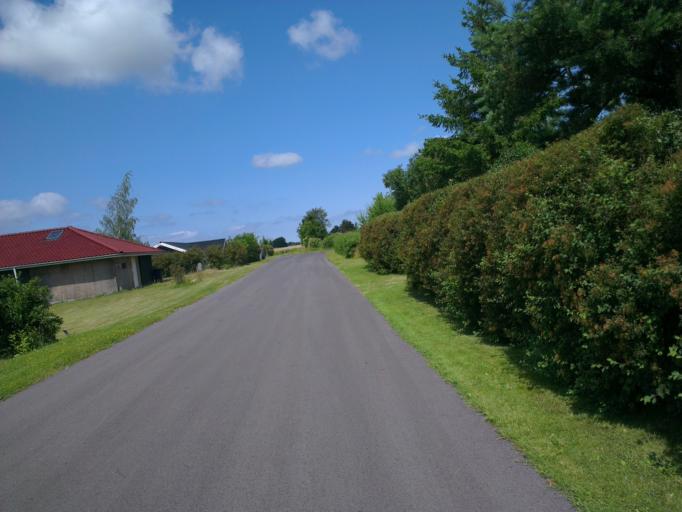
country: DK
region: Zealand
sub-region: Lejre Kommune
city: Ejby
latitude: 55.7500
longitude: 11.8701
